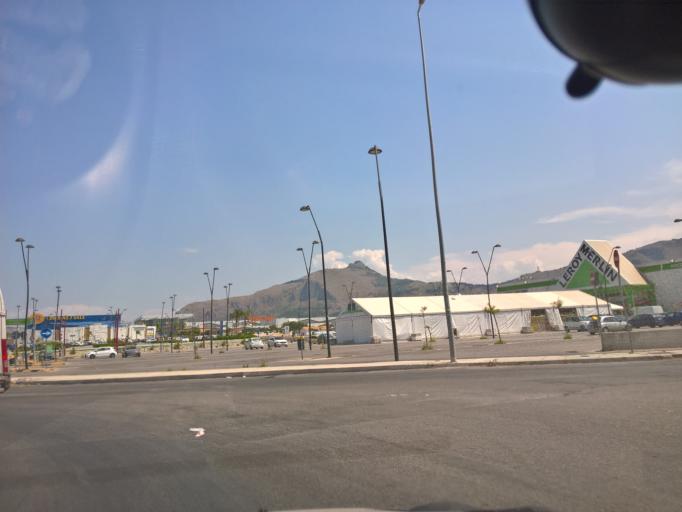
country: IT
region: Sicily
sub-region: Palermo
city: Ciaculli
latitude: 38.0916
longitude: 13.4094
